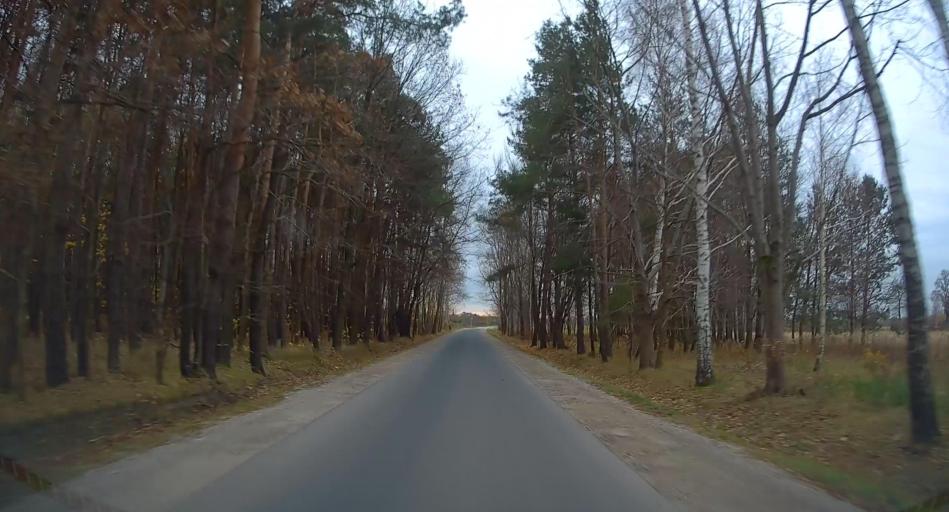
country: PL
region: Lodz Voivodeship
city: Zabia Wola
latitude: 52.0103
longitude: 20.6552
